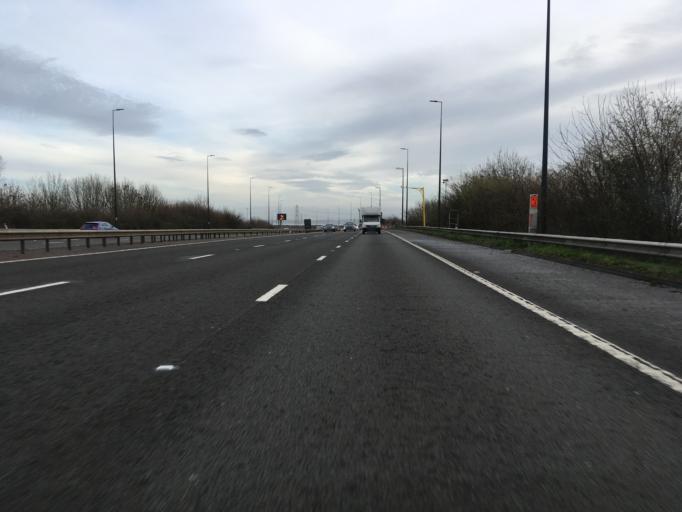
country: GB
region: Wales
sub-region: Monmouthshire
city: Rogiet
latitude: 51.5845
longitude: -2.7979
